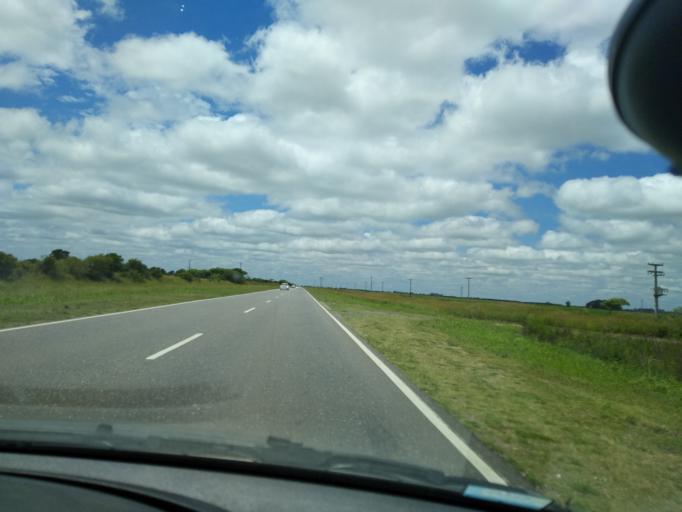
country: AR
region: Cordoba
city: Toledo
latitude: -31.6466
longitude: -64.0544
